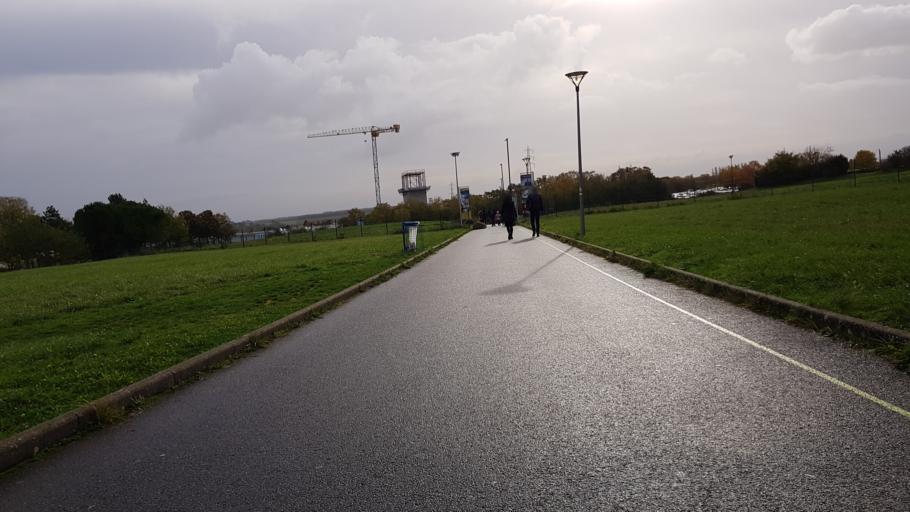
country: FR
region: Poitou-Charentes
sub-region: Departement de la Vienne
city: Chasseneuil-du-Poitou
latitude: 46.6673
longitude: 0.3641
